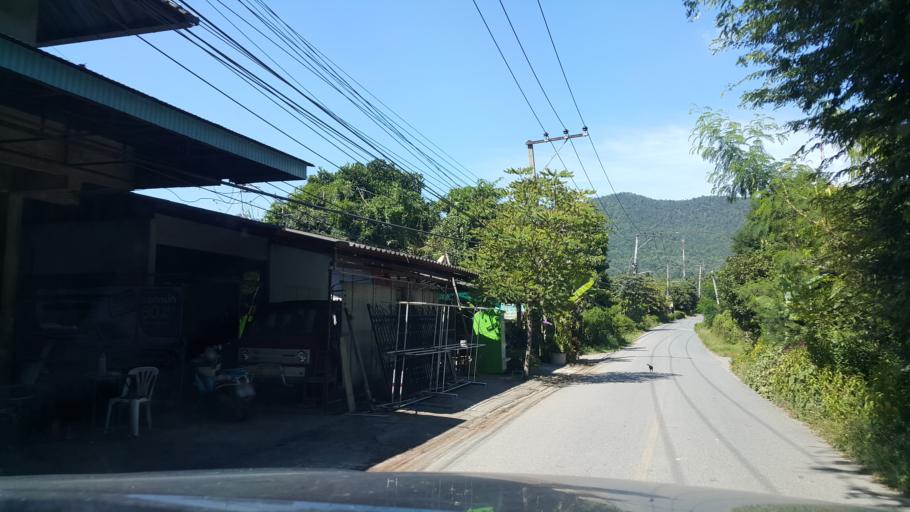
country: TH
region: Chiang Mai
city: Mae On
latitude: 18.7381
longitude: 99.2074
